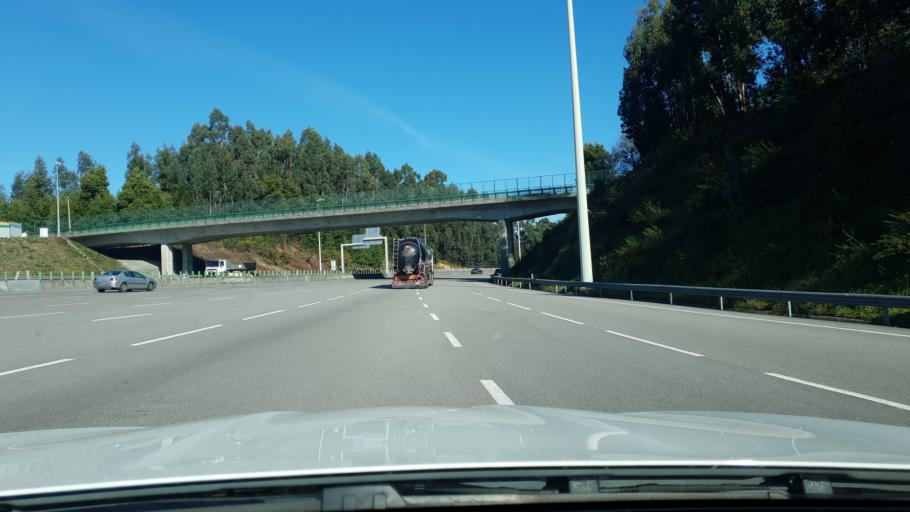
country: PT
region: Porto
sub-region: Vila Nova de Gaia
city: Grijo
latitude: 41.0184
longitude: -8.5808
